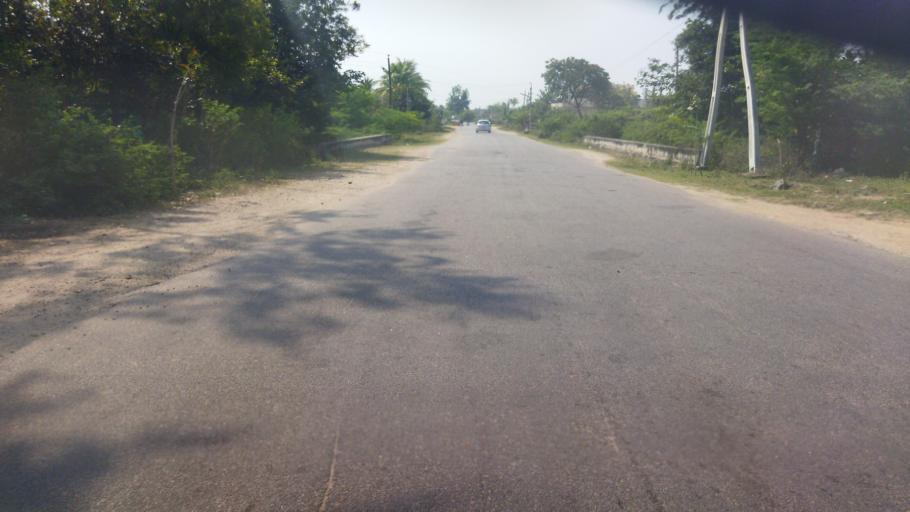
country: IN
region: Telangana
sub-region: Nalgonda
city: Nalgonda
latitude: 17.1539
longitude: 79.3113
